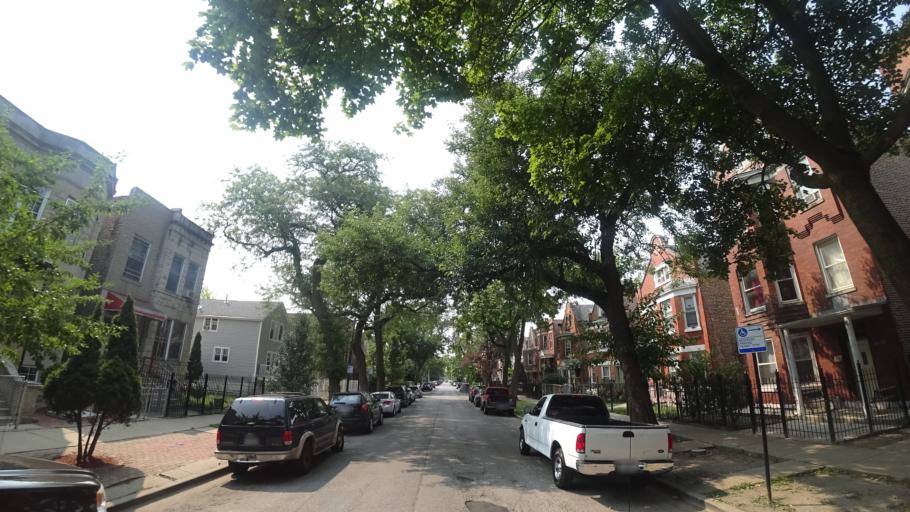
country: US
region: Illinois
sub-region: Cook County
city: Cicero
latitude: 41.8473
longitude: -87.7198
